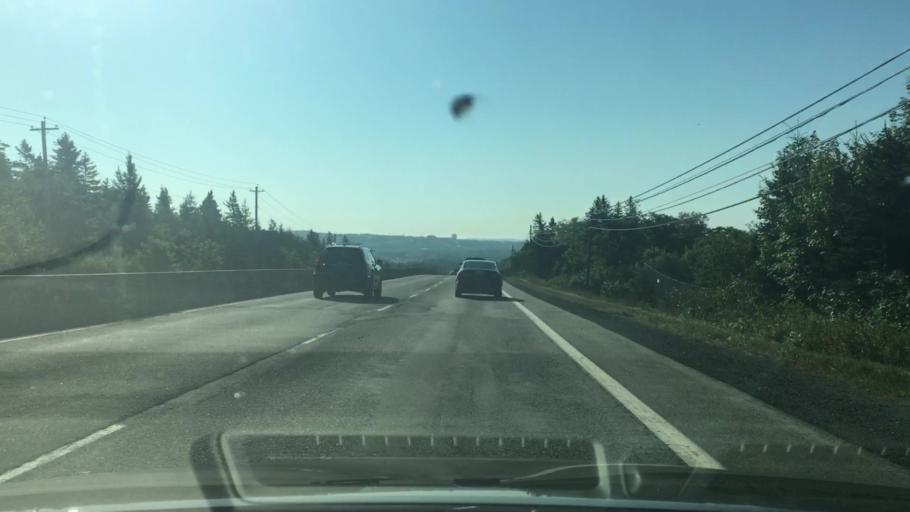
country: CA
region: Nova Scotia
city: Dartmouth
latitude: 44.7169
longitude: -63.6338
